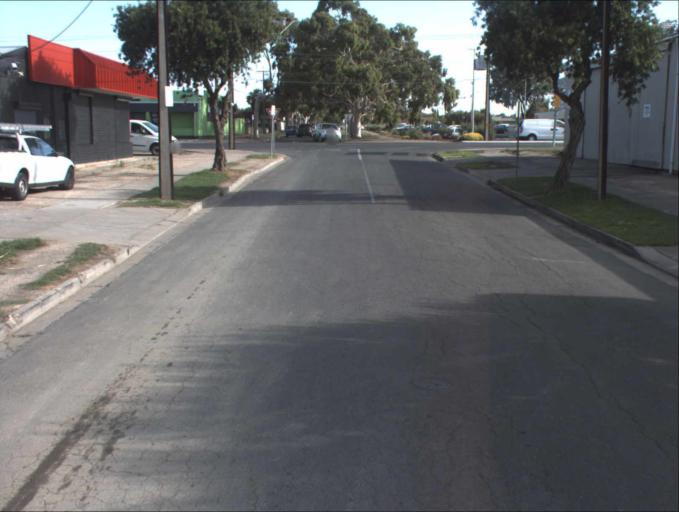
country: AU
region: South Australia
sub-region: Port Adelaide Enfield
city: Klemzig
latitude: -34.8718
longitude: 138.6342
